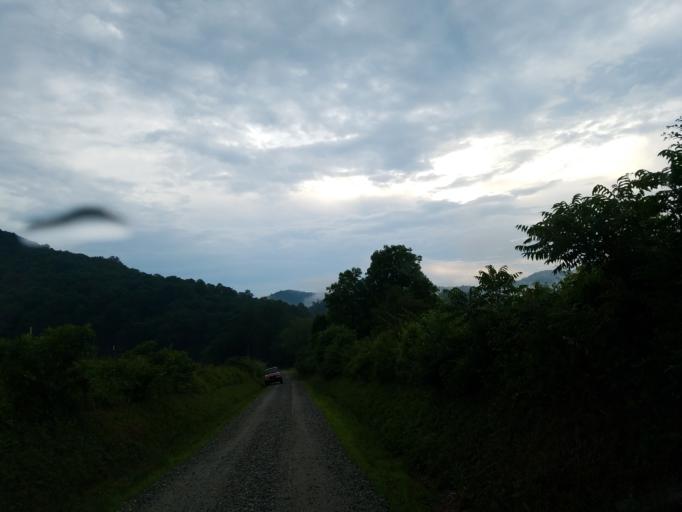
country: US
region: Georgia
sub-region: Lumpkin County
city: Dahlonega
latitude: 34.6945
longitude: -84.0742
